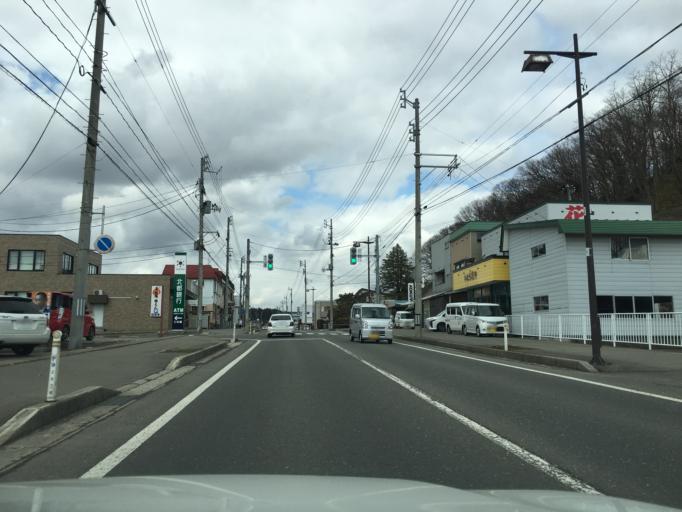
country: JP
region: Akita
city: Hanawa
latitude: 40.2689
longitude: 140.7692
